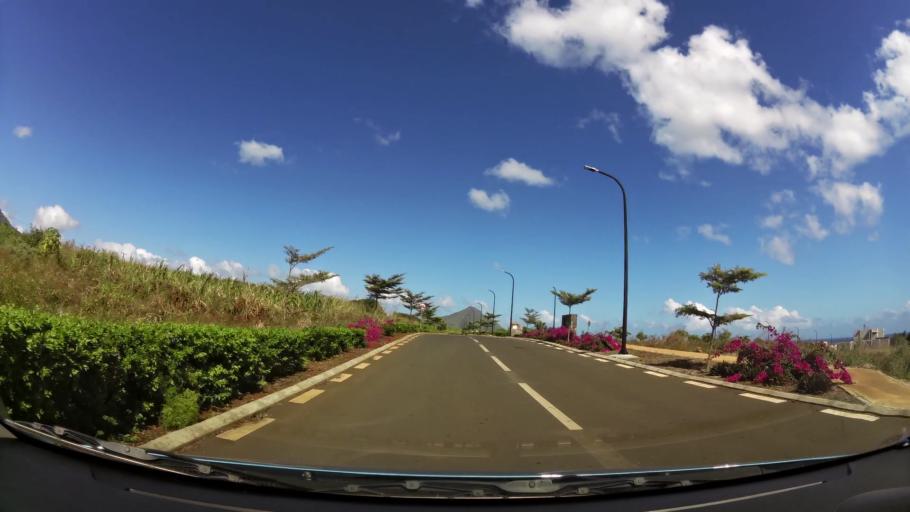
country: MU
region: Black River
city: Cascavelle
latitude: -20.2810
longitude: 57.3920
